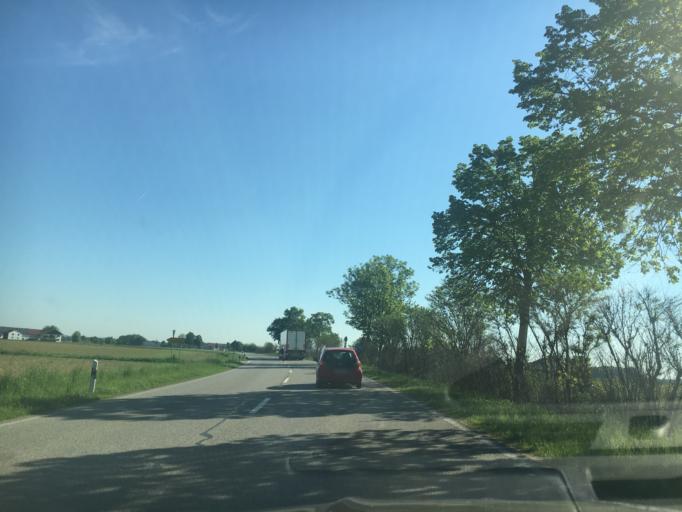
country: DE
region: Bavaria
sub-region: Upper Bavaria
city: Unterneukirchen
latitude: 48.1904
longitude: 12.6396
